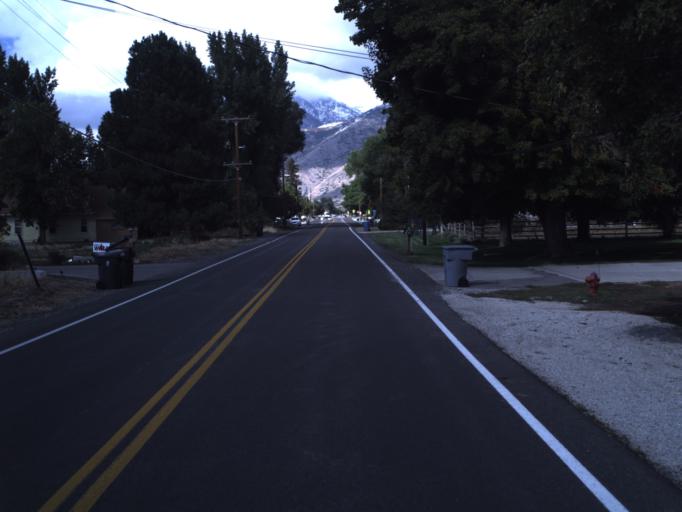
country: US
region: Utah
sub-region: Utah County
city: Mapleton
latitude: 40.1269
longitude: -111.5788
